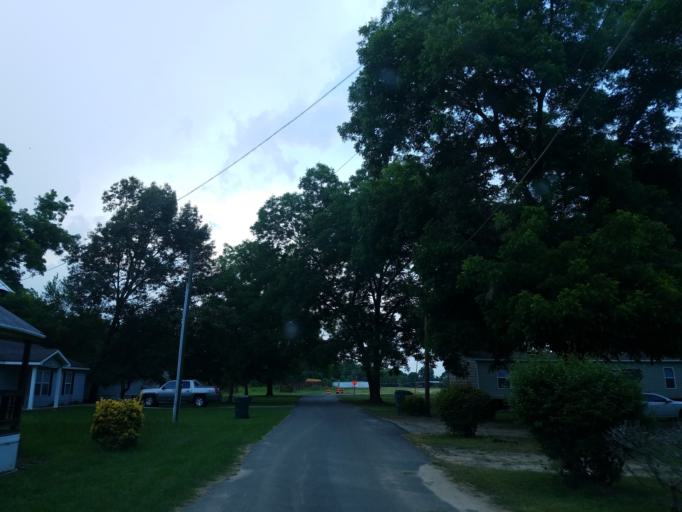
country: US
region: Georgia
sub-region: Dooly County
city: Unadilla
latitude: 32.1908
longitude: -83.7589
